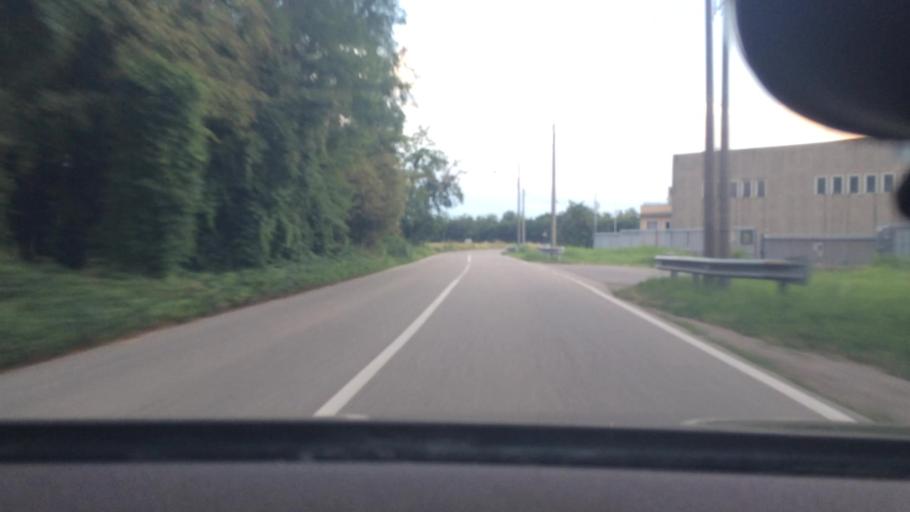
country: IT
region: Lombardy
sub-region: Citta metropolitana di Milano
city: Vanzago
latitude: 45.5194
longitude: 8.9858
